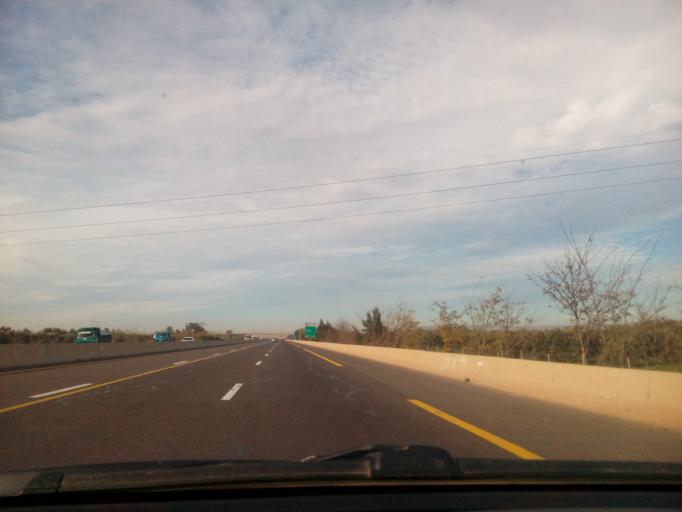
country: DZ
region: Mascara
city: Sig
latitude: 35.5814
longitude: -0.2322
